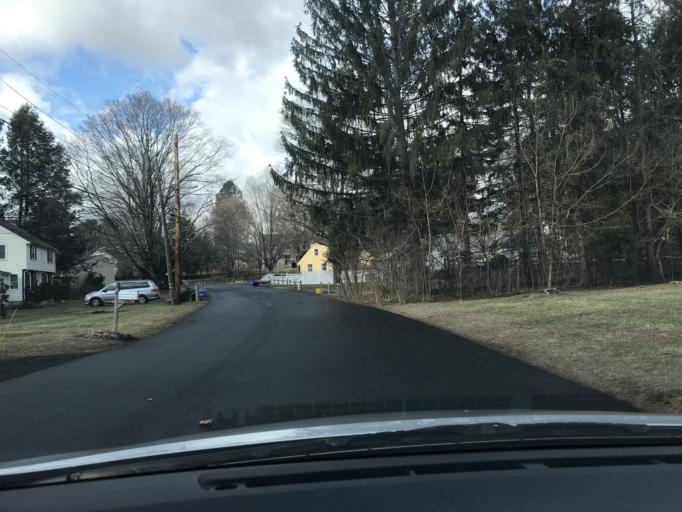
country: US
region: Massachusetts
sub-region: Middlesex County
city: Lexington
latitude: 42.4696
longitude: -71.2255
